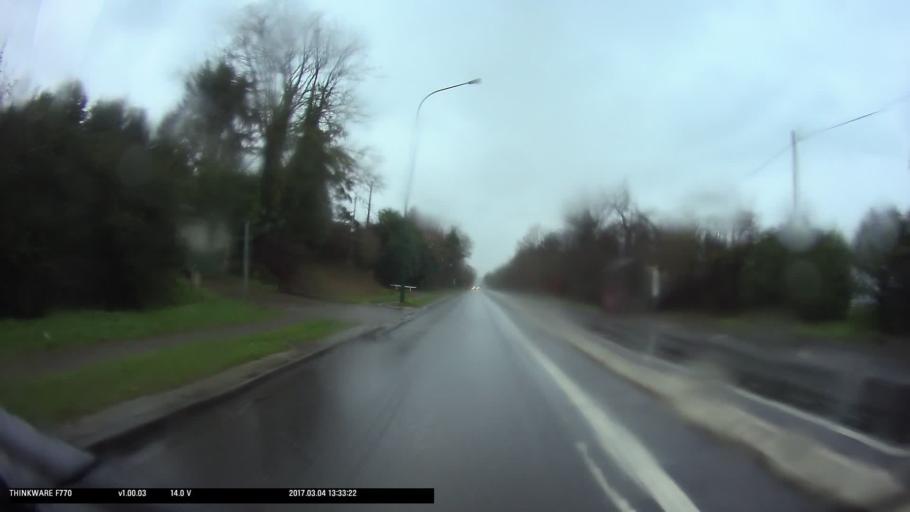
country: FR
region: Ile-de-France
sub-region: Departement du Val-d'Oise
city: Marines
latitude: 49.1257
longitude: 2.0001
